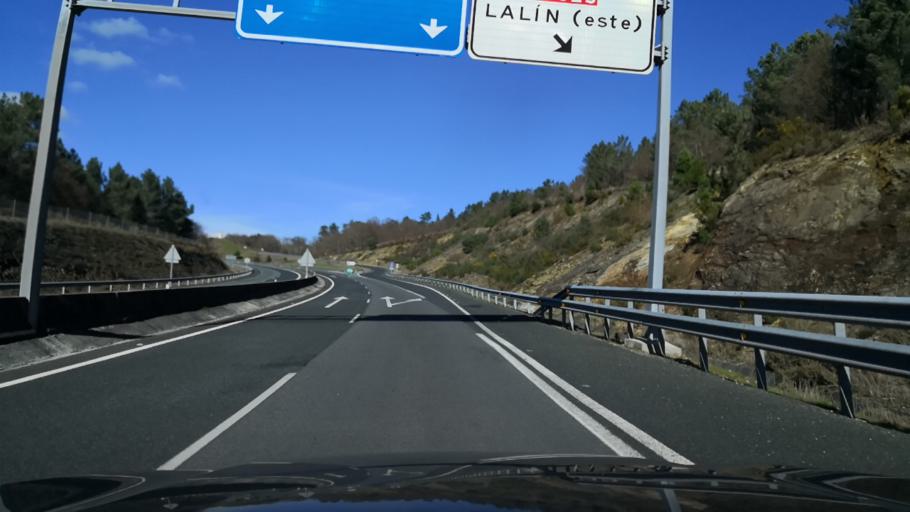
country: ES
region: Galicia
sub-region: Provincia de Pontevedra
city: Lalin
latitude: 42.6159
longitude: -8.0980
